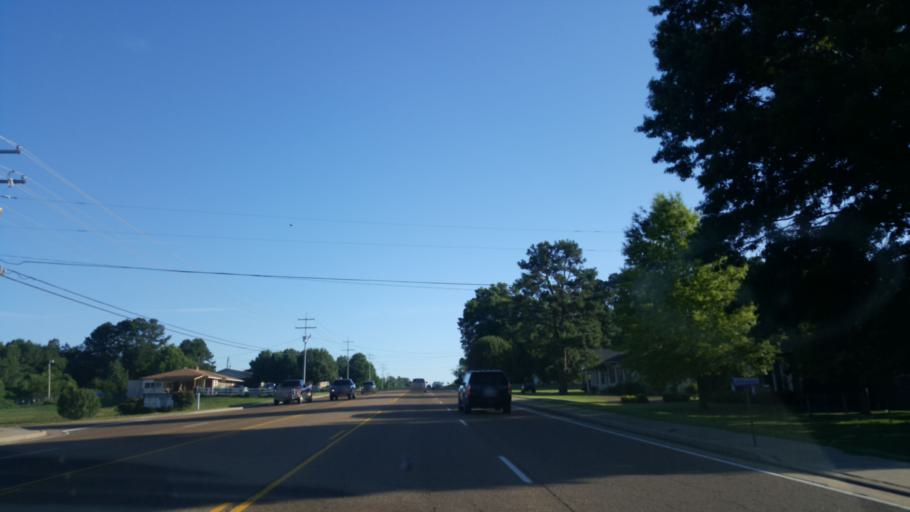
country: US
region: Tennessee
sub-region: Henderson County
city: Lexington
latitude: 35.6777
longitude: -88.3853
